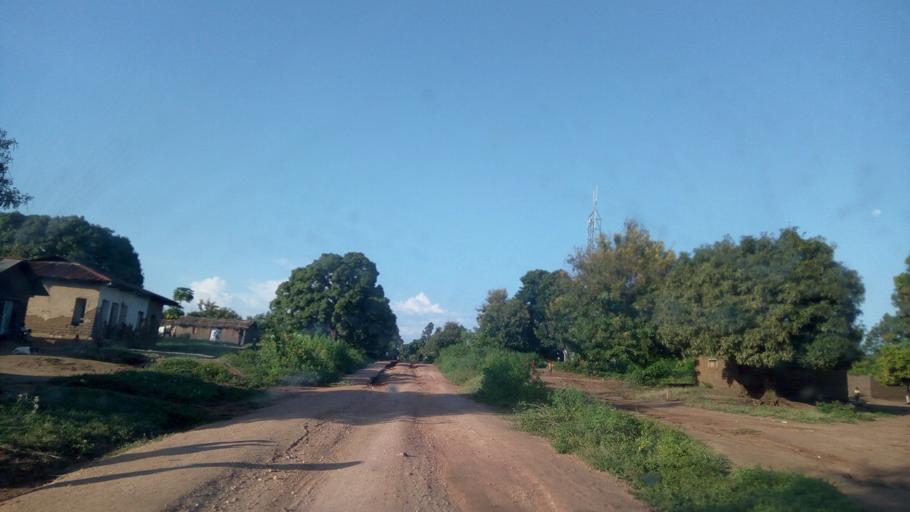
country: BI
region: Bururi
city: Rumonge
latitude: -4.1883
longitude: 29.0529
